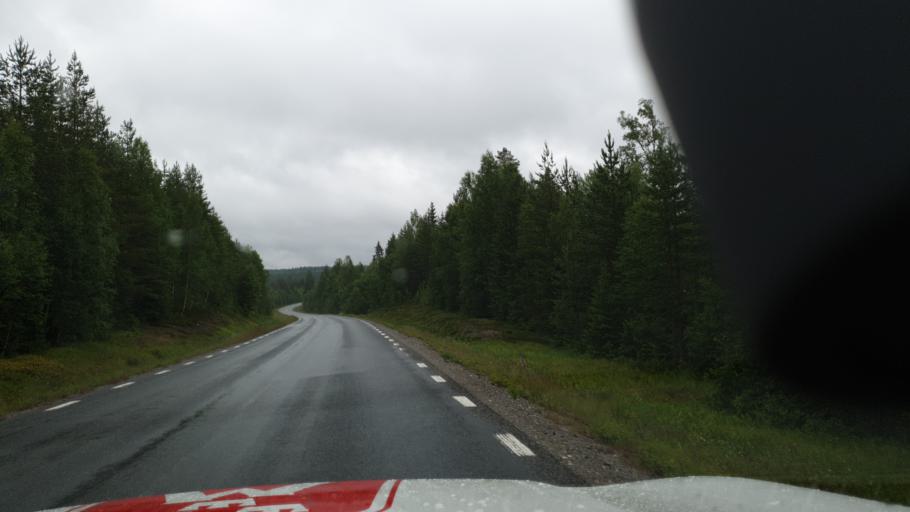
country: SE
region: Vaesterbotten
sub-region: Vannas Kommun
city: Vaennaes
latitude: 63.7797
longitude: 19.7354
